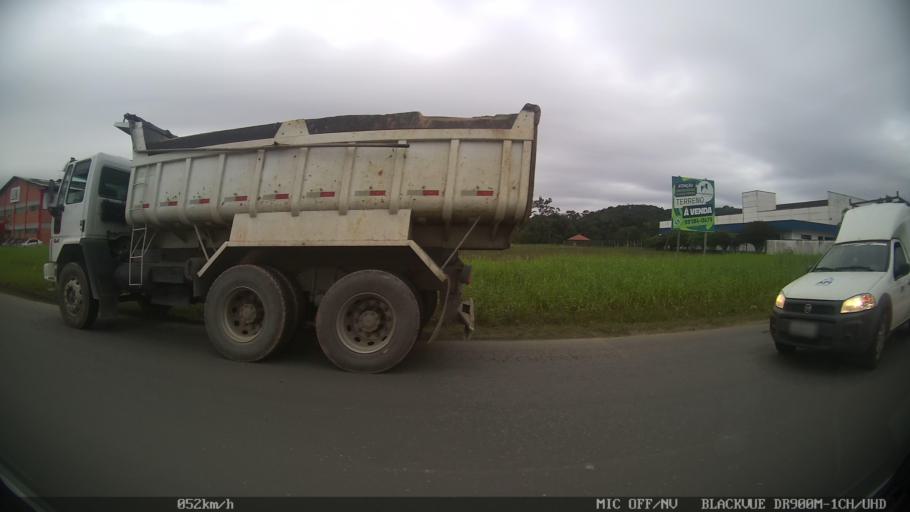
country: BR
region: Santa Catarina
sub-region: Joinville
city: Joinville
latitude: -26.2316
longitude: -48.9014
